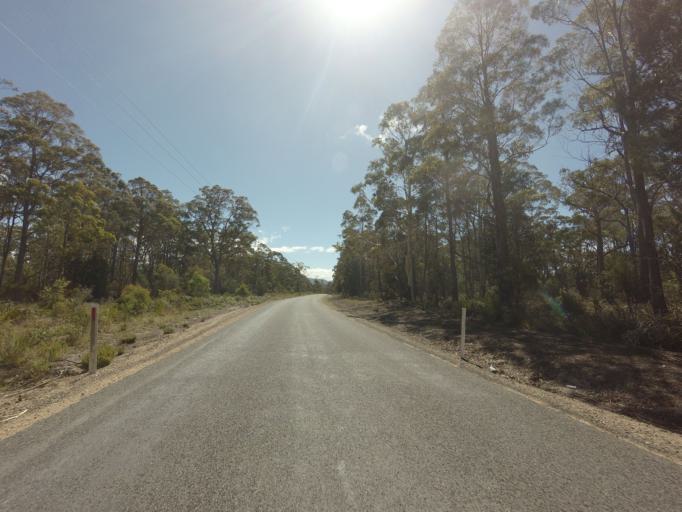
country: AU
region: Tasmania
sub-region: Break O'Day
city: St Helens
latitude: -41.6021
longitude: 148.2049
